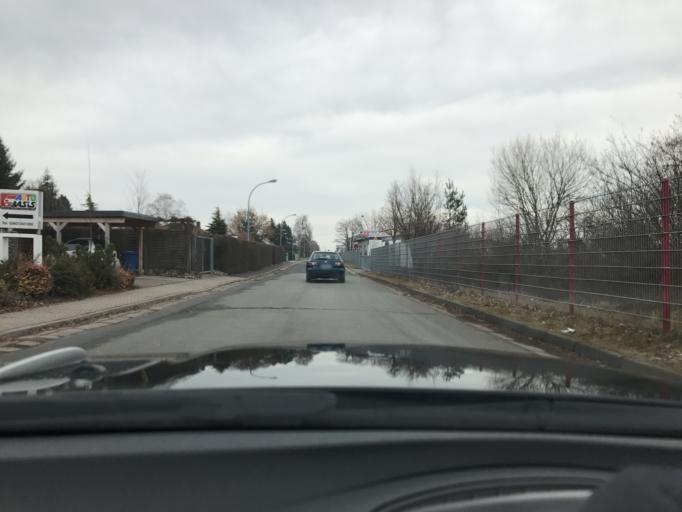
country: DE
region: Thuringia
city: Muehlhausen
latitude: 51.2015
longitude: 10.4766
